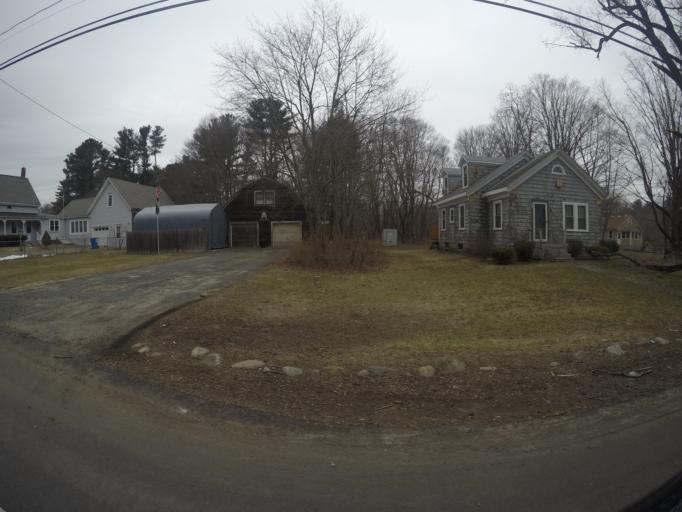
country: US
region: Massachusetts
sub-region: Bristol County
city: Easton
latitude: 42.0400
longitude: -71.0689
